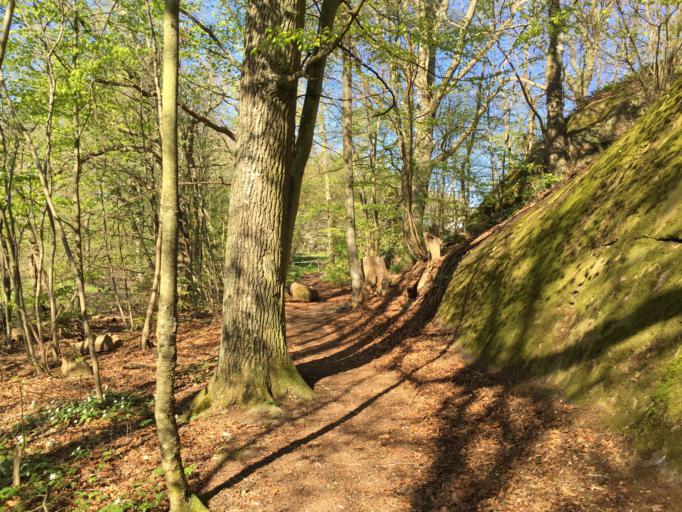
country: SE
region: Blekinge
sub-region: Karlskrona Kommun
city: Rodeby
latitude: 56.1995
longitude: 15.6644
